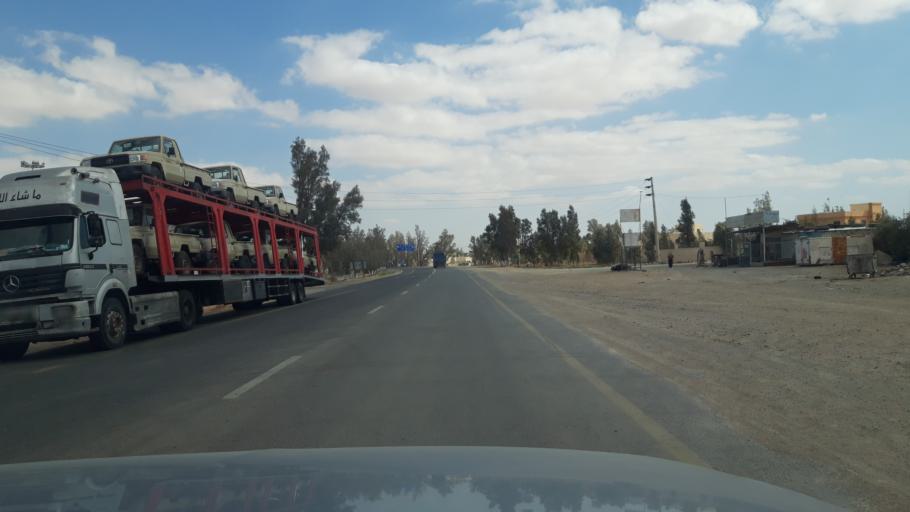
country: JO
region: Amman
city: Al Azraq ash Shamali
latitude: 31.8388
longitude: 36.8098
